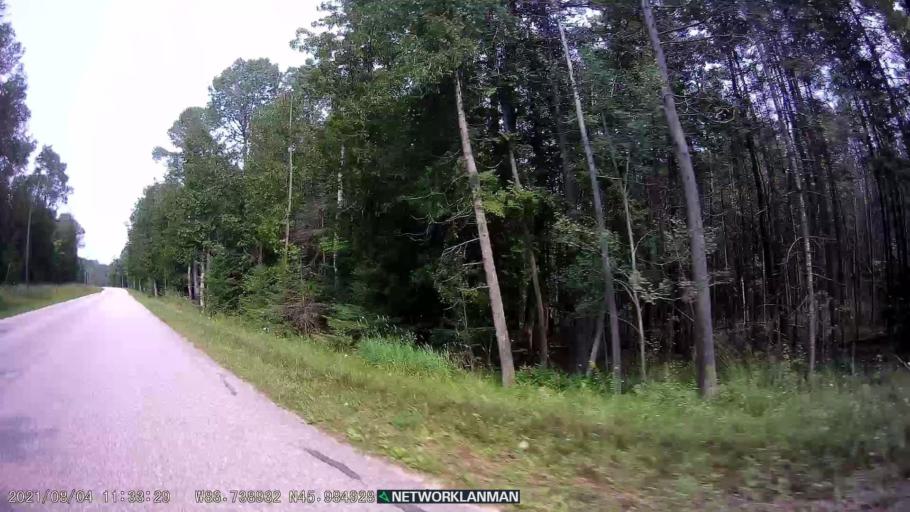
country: CA
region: Ontario
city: Thessalon
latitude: 45.9853
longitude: -83.7391
